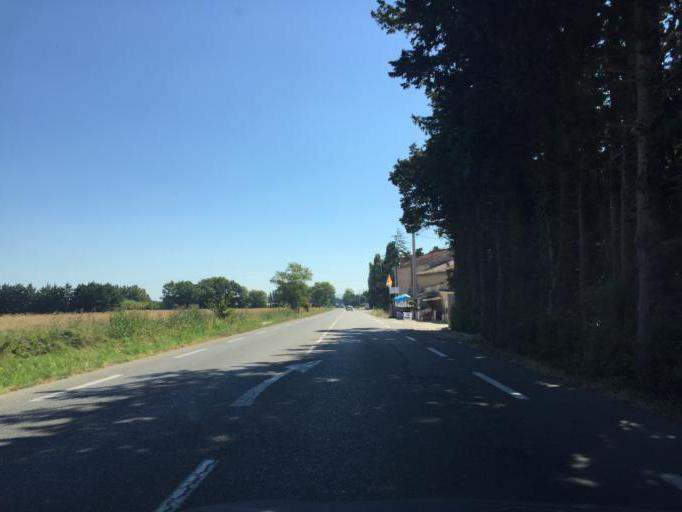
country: FR
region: Provence-Alpes-Cote d'Azur
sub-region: Departement du Vaucluse
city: L'Isle-sur-la-Sorgue
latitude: 43.8798
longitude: 5.0181
